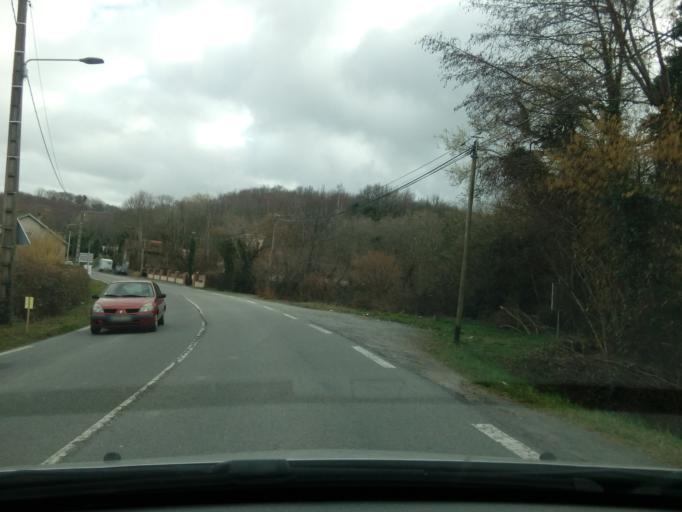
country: FR
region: Limousin
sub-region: Departement de la Creuse
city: Gueret
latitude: 46.1627
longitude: 1.8903
